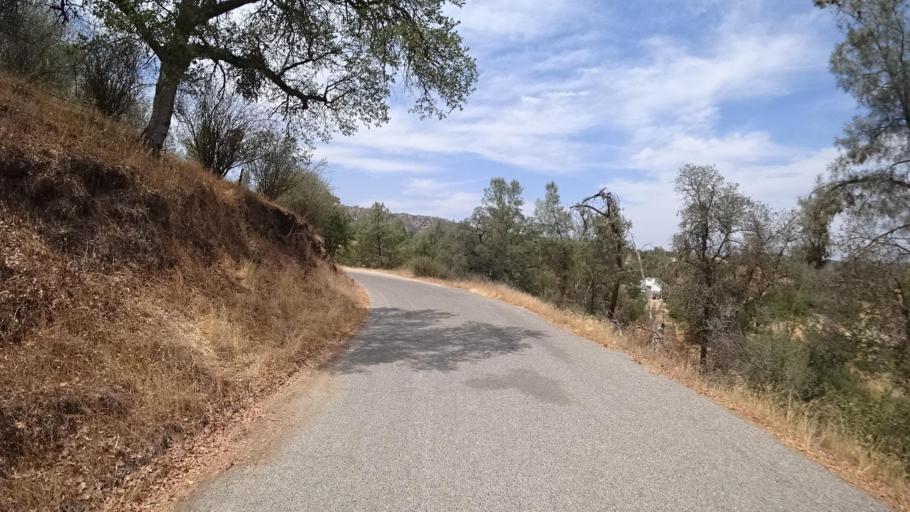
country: US
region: California
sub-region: Madera County
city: Yosemite Lakes
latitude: 37.2970
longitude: -119.8692
